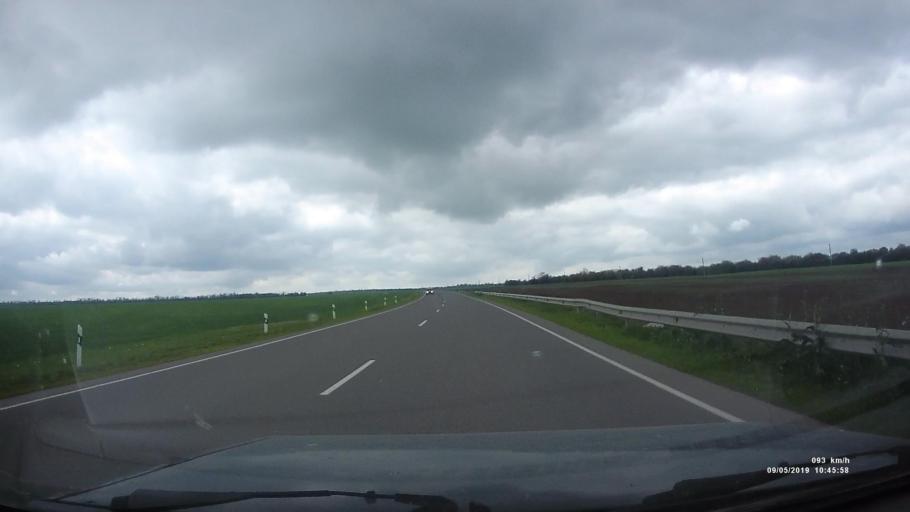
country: RU
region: Rostov
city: Peshkovo
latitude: 46.9897
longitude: 39.3596
